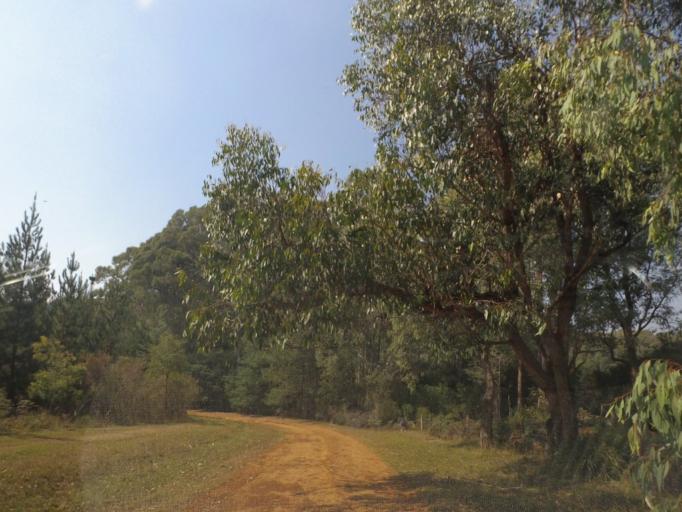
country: AU
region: Victoria
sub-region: Yarra Ranges
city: Healesville
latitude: -37.5601
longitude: 145.6433
